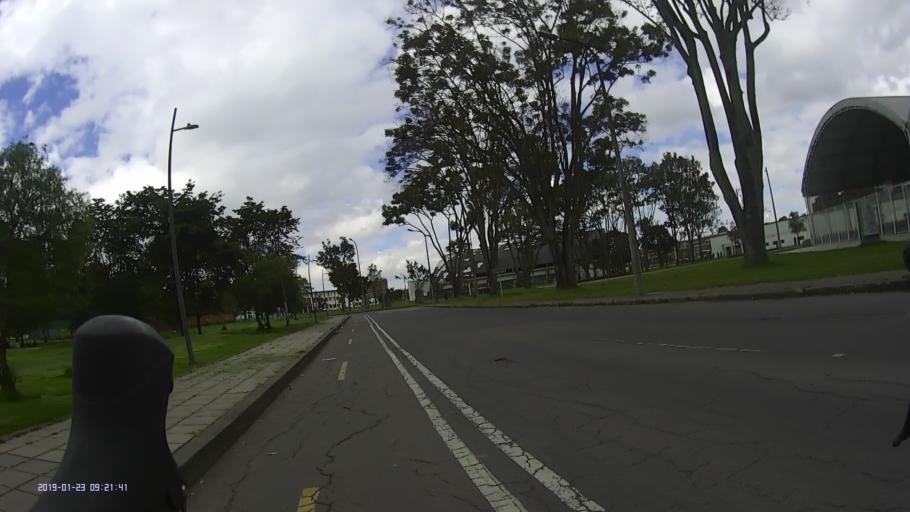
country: CO
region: Bogota D.C.
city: Bogota
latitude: 4.6397
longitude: -74.0844
